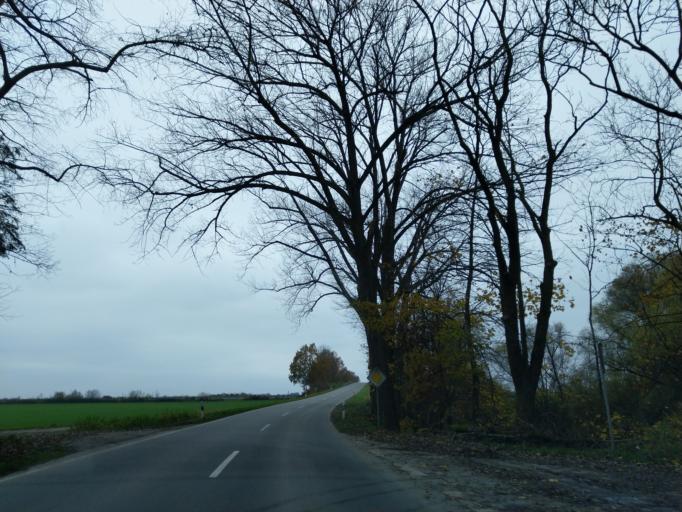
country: DE
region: Bavaria
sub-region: Lower Bavaria
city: Otzing
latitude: 48.7662
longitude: 12.7816
